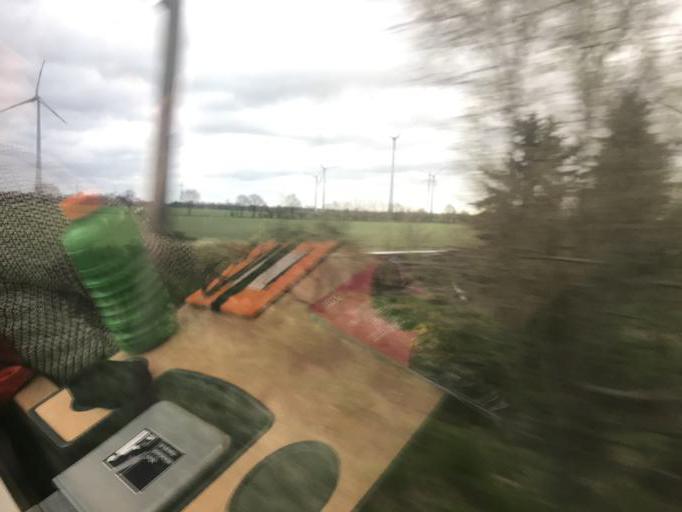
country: DE
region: Schleswig-Holstein
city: Hasenkrug
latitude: 54.0045
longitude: 9.8519
